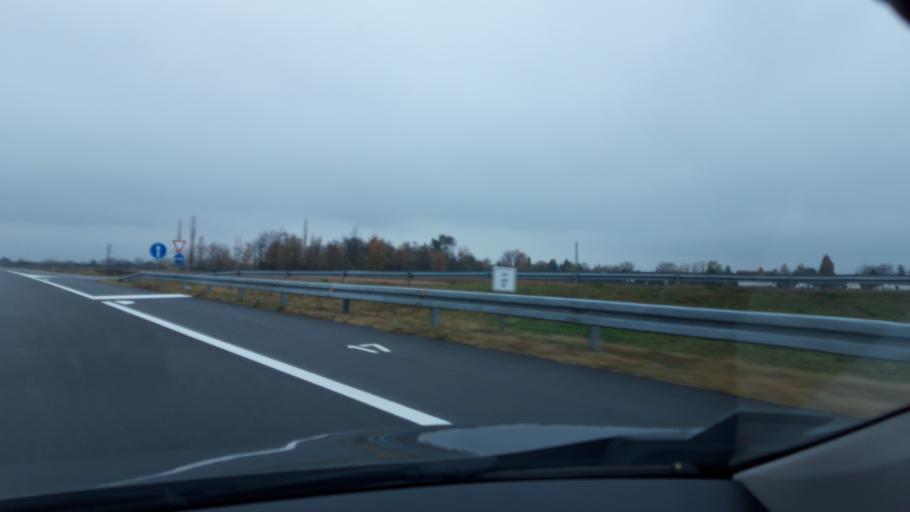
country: HU
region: Csongrad
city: Asotthalom
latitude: 46.1053
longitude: 19.7939
